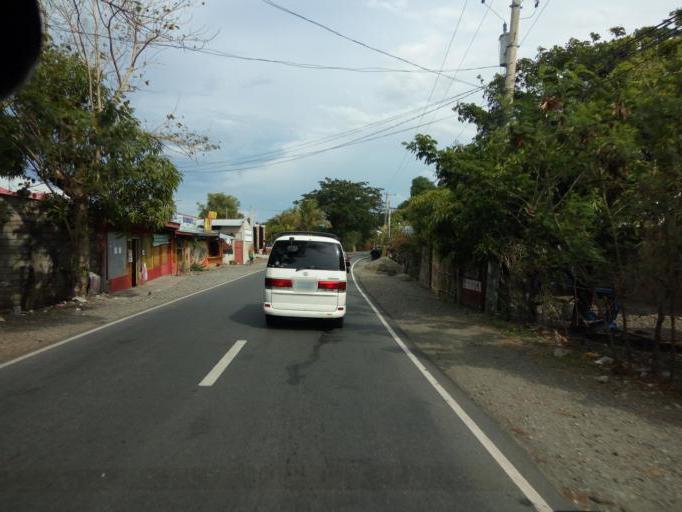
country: PH
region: Central Luzon
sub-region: Province of Nueva Ecija
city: Sibul
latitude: 15.8071
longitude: 120.9696
